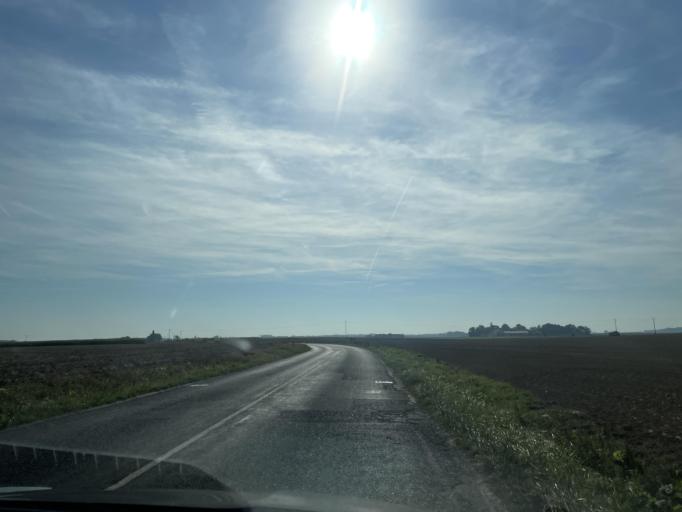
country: FR
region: Ile-de-France
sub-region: Departement de Seine-et-Marne
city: Sammeron
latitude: 48.8844
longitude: 3.0692
